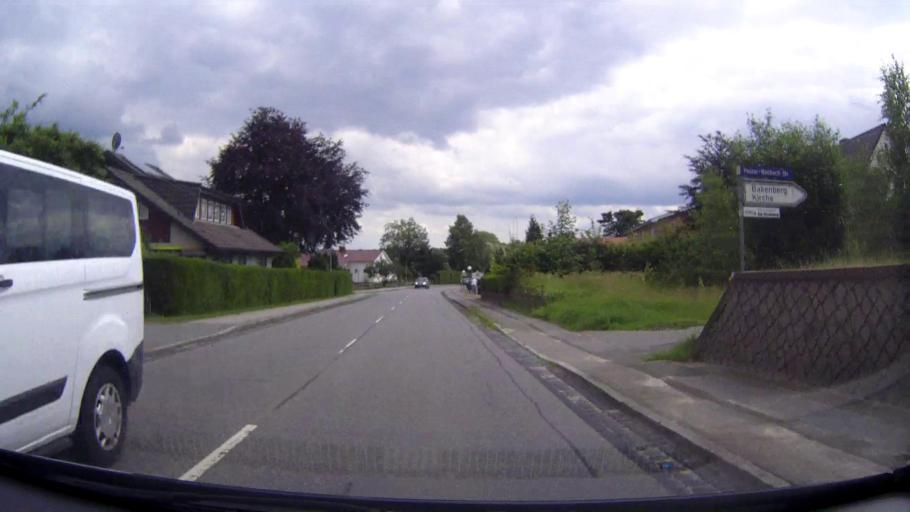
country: DE
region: Schleswig-Holstein
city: Gokels
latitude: 54.1128
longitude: 9.4680
